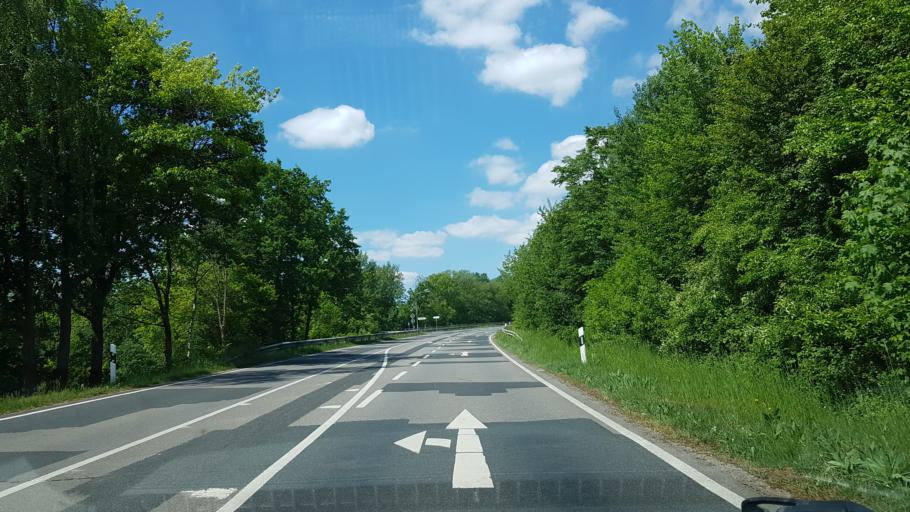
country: DE
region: Lower Saxony
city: Eschede
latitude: 52.7401
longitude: 10.2373
